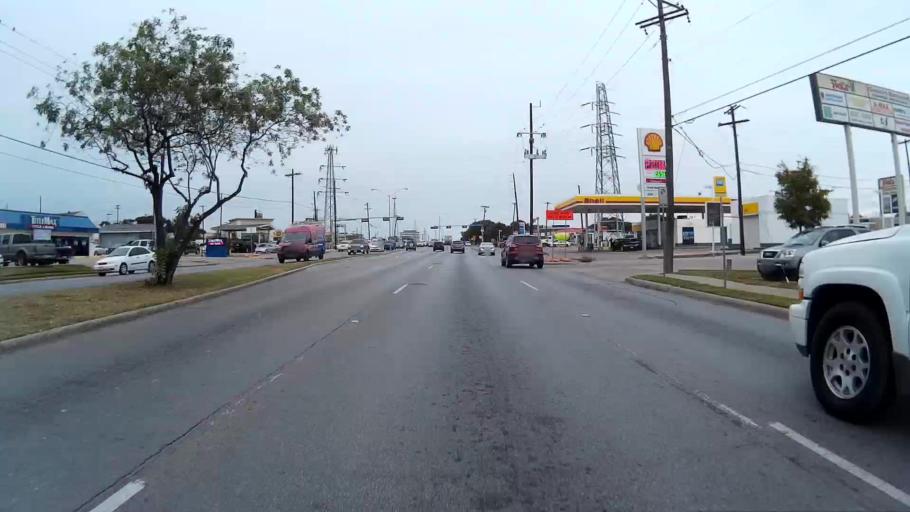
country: US
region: Texas
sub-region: Dallas County
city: Richardson
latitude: 32.9390
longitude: -96.7689
